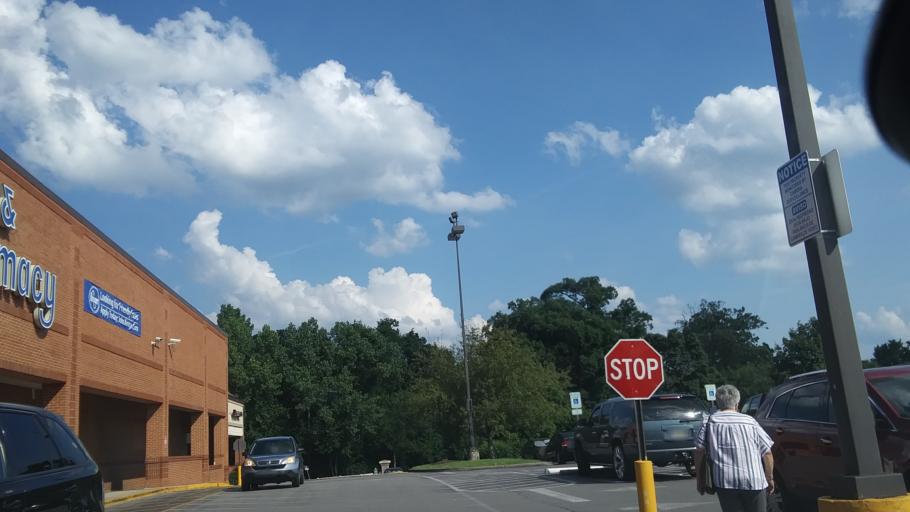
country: US
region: Tennessee
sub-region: Rutherford County
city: La Vergne
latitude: 36.0883
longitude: -86.6476
